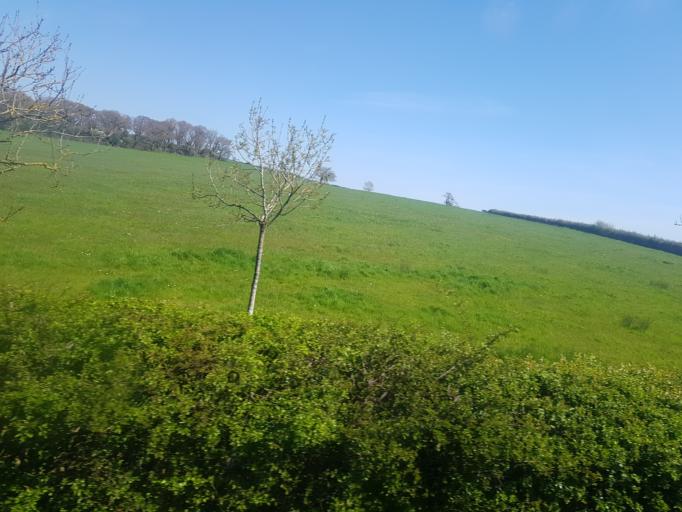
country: GB
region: England
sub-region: Isle of Wight
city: East Cowes
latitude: 50.7320
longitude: -1.2672
